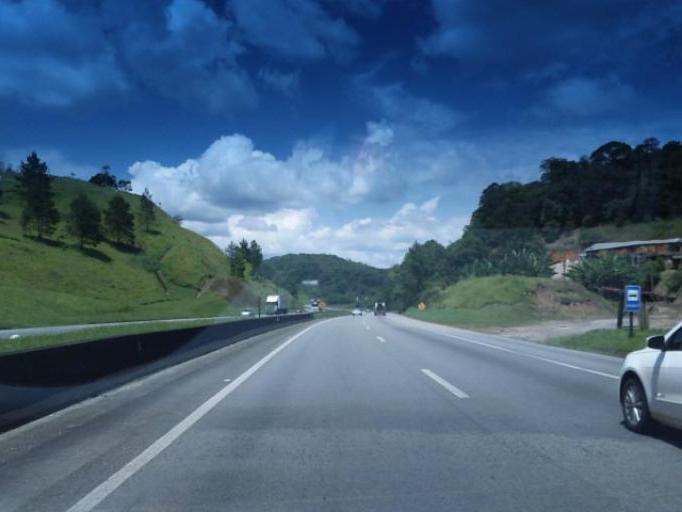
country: BR
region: Sao Paulo
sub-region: Juquitiba
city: Juquitiba
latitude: -23.9415
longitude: -47.0924
